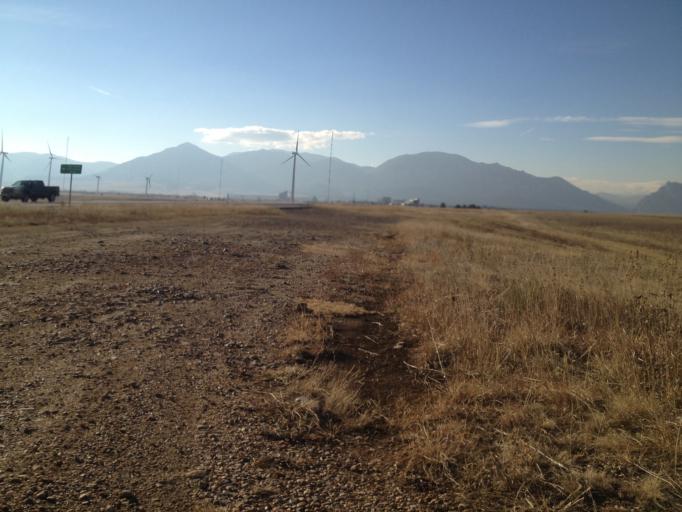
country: US
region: Colorado
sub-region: Boulder County
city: Superior
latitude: 39.9141
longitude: -105.2084
